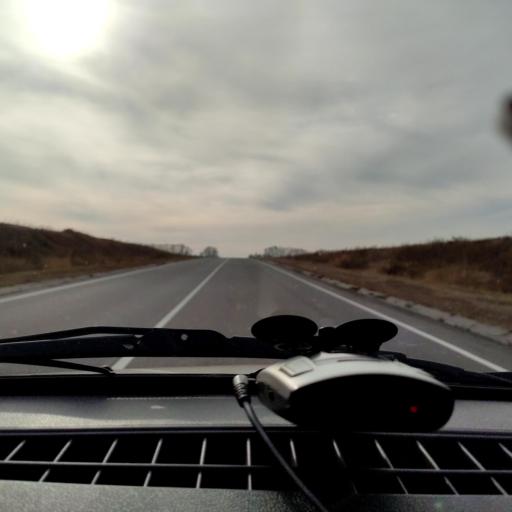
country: RU
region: Voronezj
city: Strelitsa
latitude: 51.5179
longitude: 38.9677
